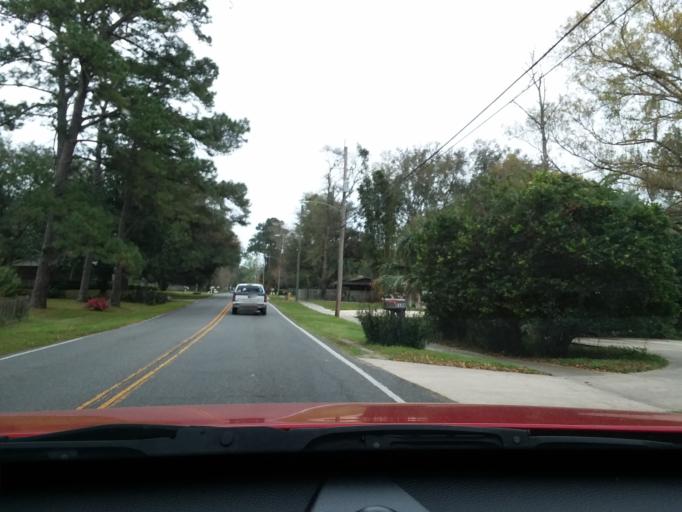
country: US
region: Florida
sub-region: Duval County
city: Jacksonville
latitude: 30.2944
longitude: -81.7480
